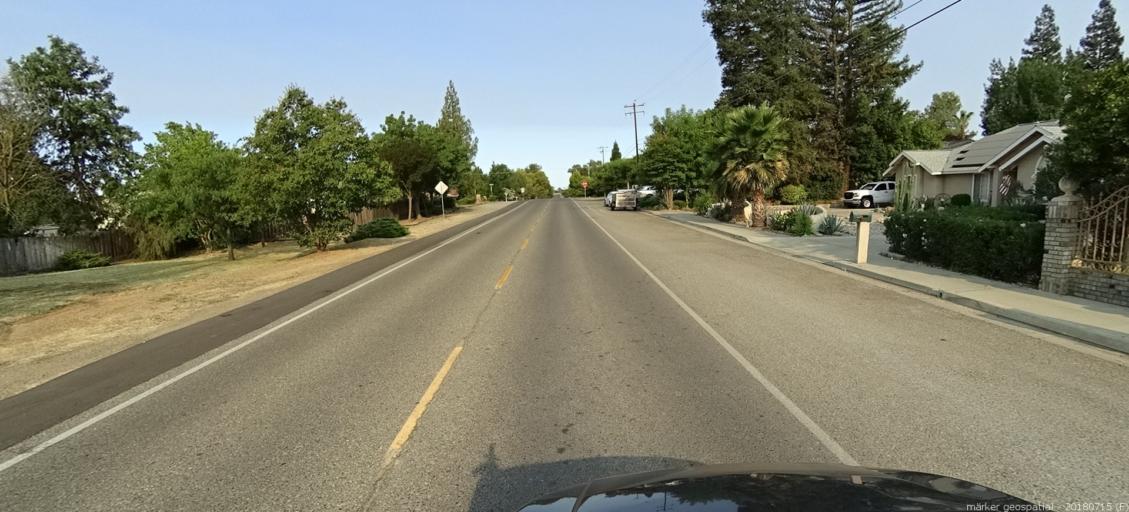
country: US
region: California
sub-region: Madera County
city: Madera Acres
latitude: 37.0247
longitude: -120.0633
